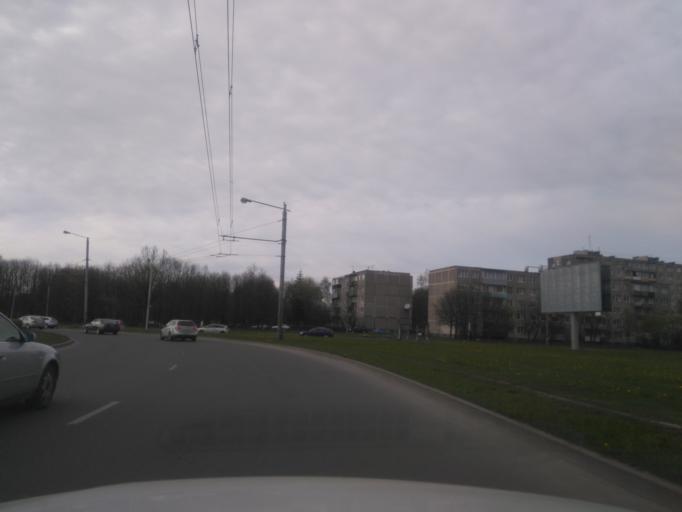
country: LT
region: Kauno apskritis
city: Dainava (Kaunas)
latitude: 54.9130
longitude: 23.9757
